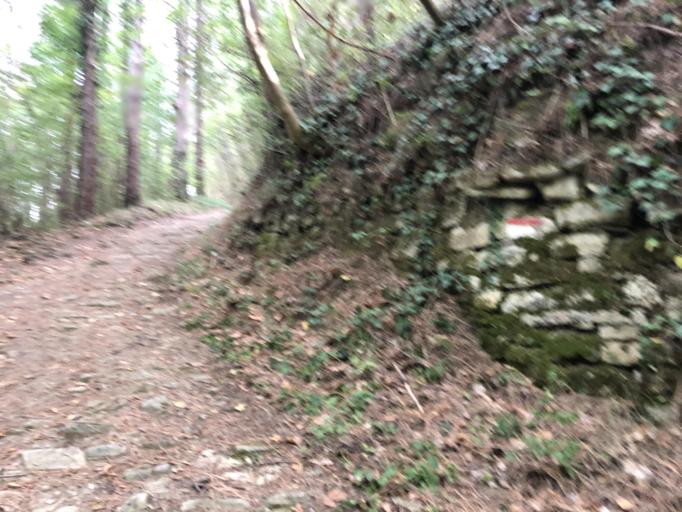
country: IT
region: Emilia-Romagna
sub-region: Forli-Cesena
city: Portico e San Benedetto
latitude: 44.0217
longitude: 11.7825
